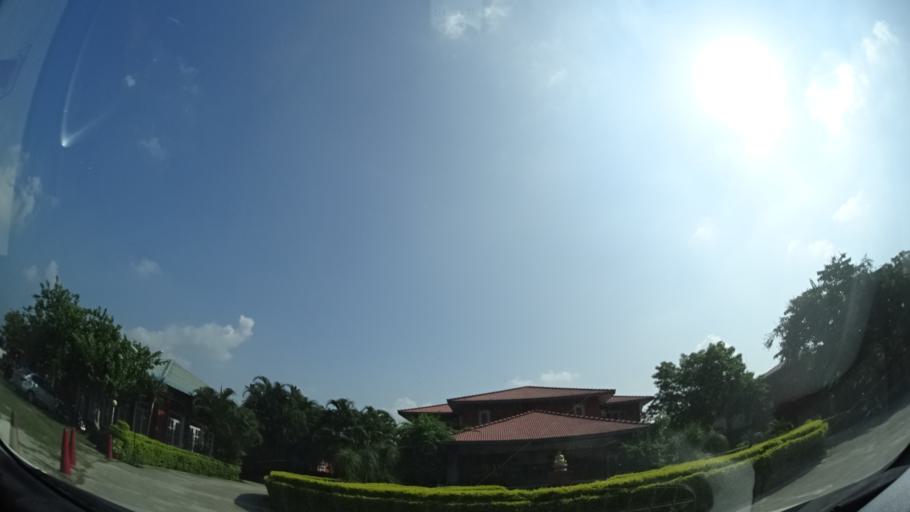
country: NP
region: Western Region
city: Butwal
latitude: 27.6220
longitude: 83.4713
